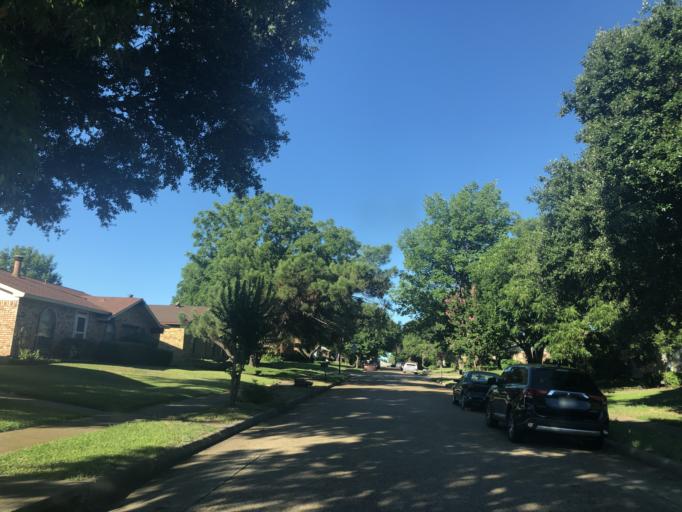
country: US
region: Texas
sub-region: Dallas County
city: Duncanville
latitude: 32.6405
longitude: -96.9511
